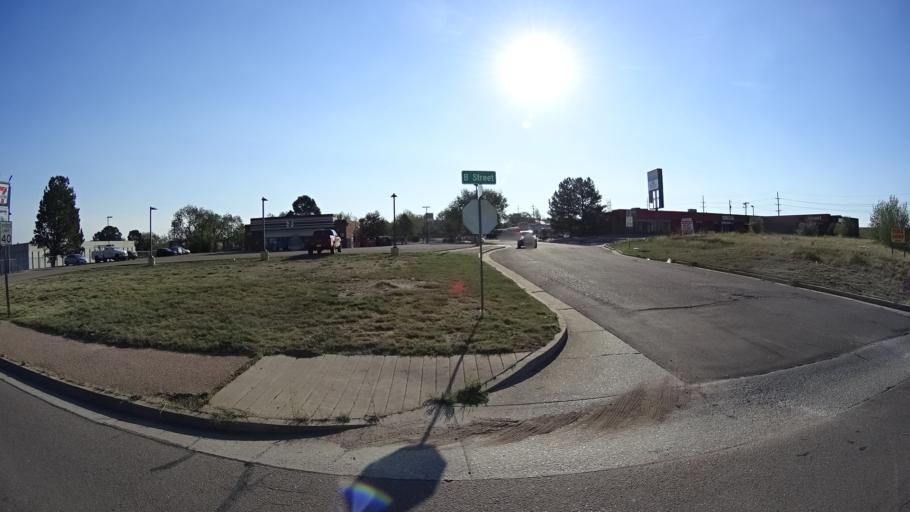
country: US
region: Colorado
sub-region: El Paso County
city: Stratmoor
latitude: 38.7672
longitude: -104.7976
